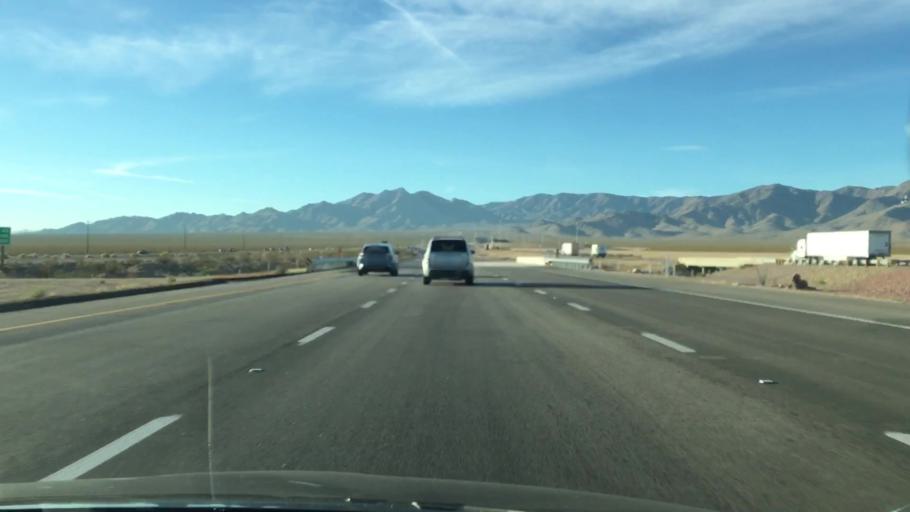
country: US
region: Nevada
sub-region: Clark County
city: Sandy Valley
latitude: 35.5142
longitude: -115.4322
